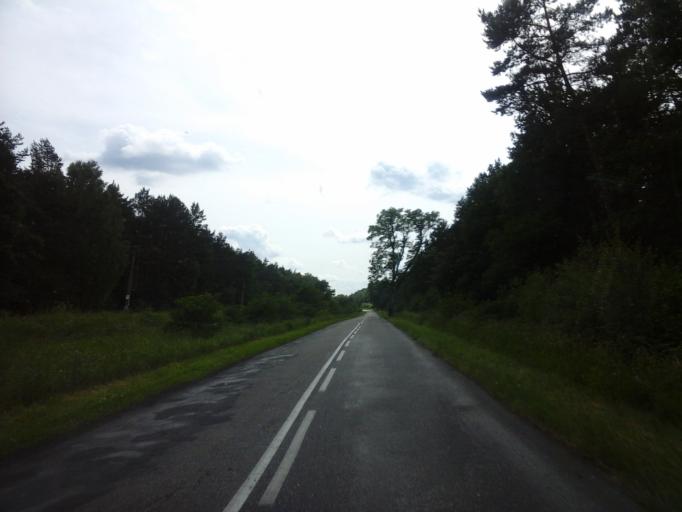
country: PL
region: West Pomeranian Voivodeship
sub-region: Powiat lobeski
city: Lobez
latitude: 53.6661
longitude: 15.6560
